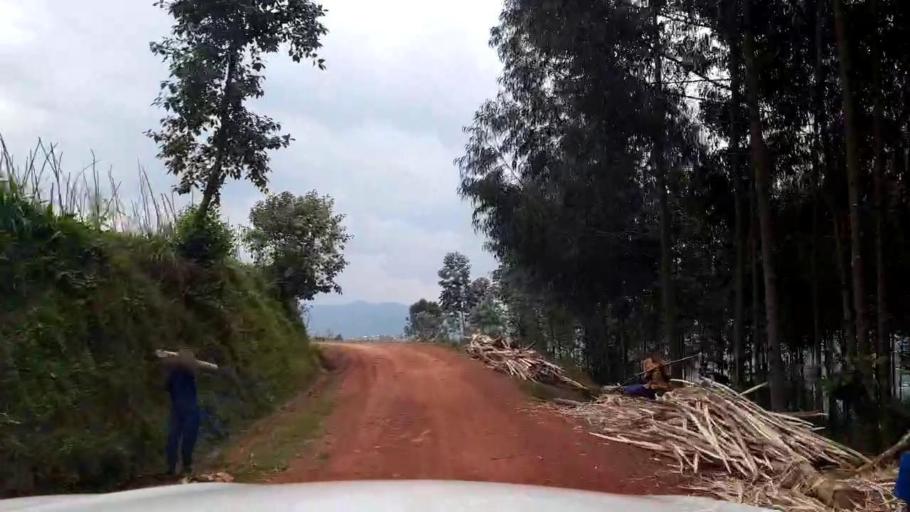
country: RW
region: Northern Province
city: Byumba
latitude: -1.5088
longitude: 29.9349
